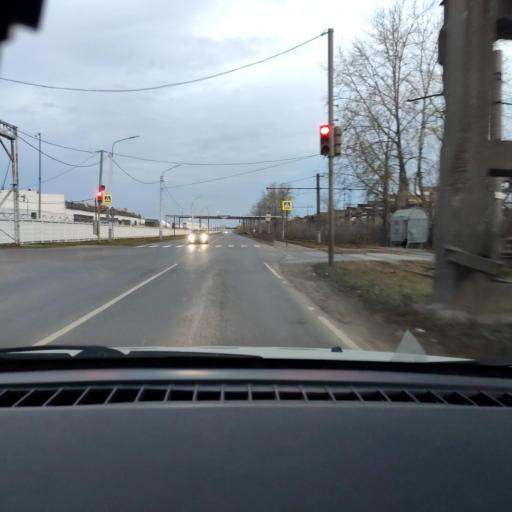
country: RU
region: Perm
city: Gamovo
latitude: 57.9140
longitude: 56.1554
